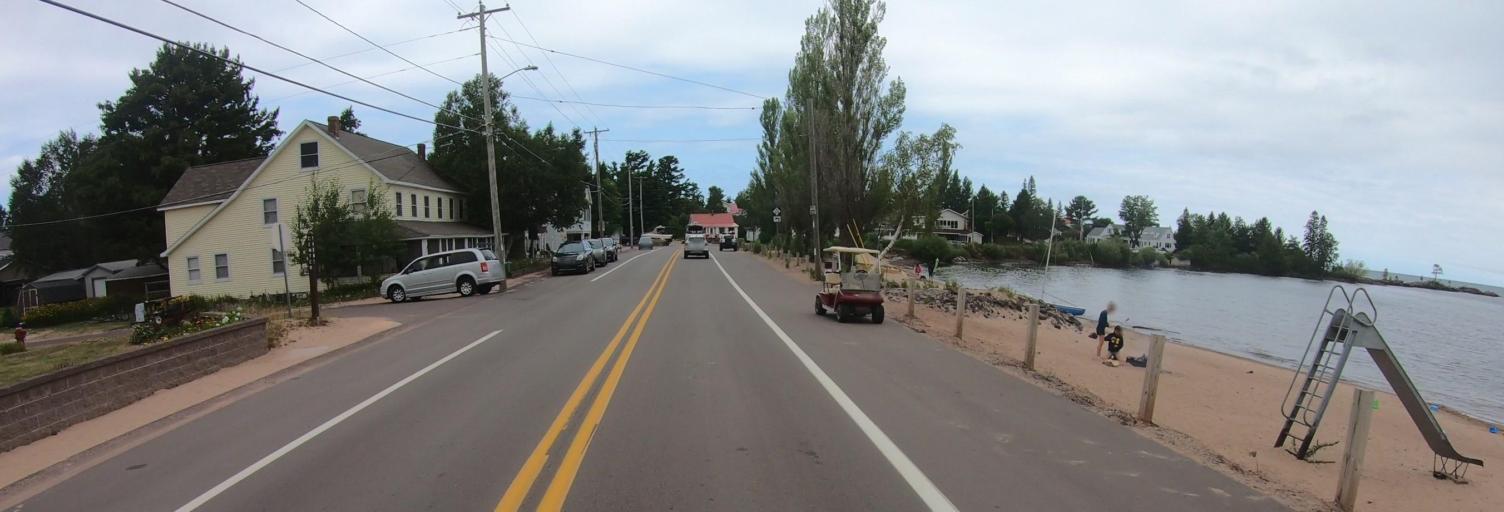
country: US
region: Michigan
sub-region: Keweenaw County
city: Eagle River
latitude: 47.4570
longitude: -88.1610
